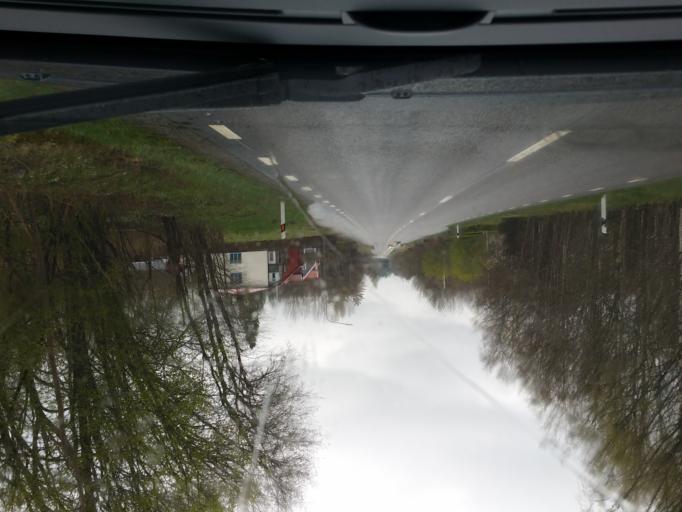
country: SE
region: Kronoberg
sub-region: Vaxjo Kommun
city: Lammhult
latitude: 57.1570
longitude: 14.5930
